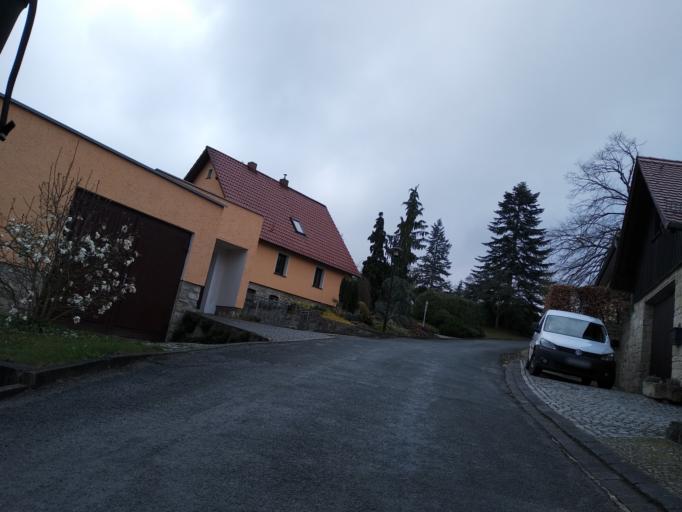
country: DE
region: Thuringia
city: Buchfart
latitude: 50.9195
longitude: 11.3324
